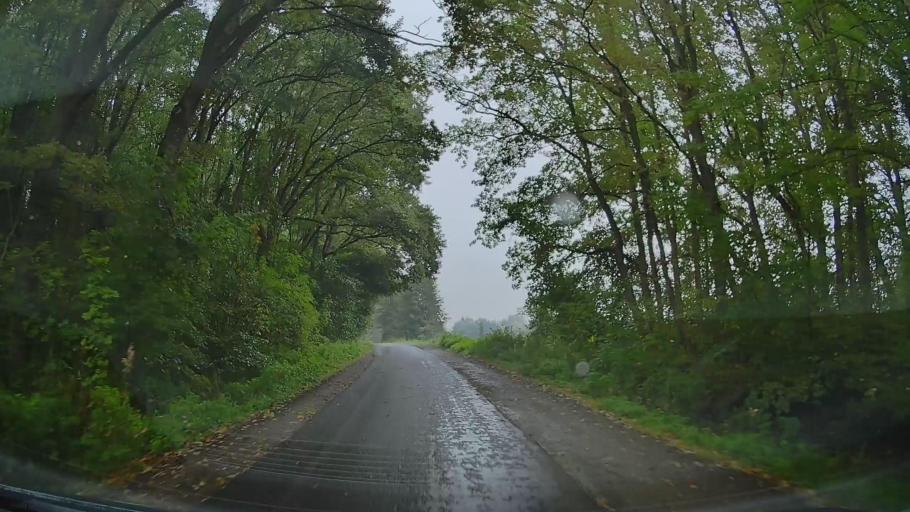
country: DE
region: Mecklenburg-Vorpommern
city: Gramkow
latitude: 53.9283
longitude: 11.3636
